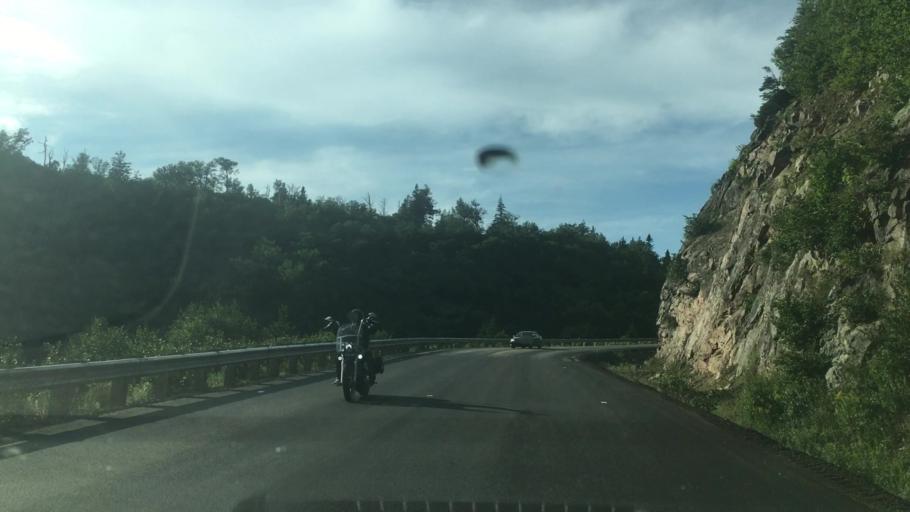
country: CA
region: Nova Scotia
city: Sydney Mines
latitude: 46.8206
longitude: -60.6535
